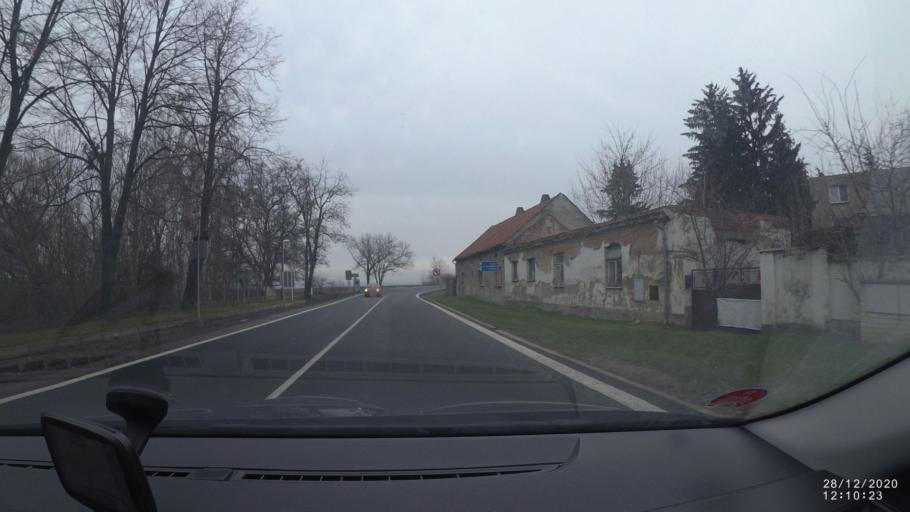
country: CZ
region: Central Bohemia
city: Brandys nad Labem-Stara Boleslav
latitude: 50.1689
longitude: 14.6315
